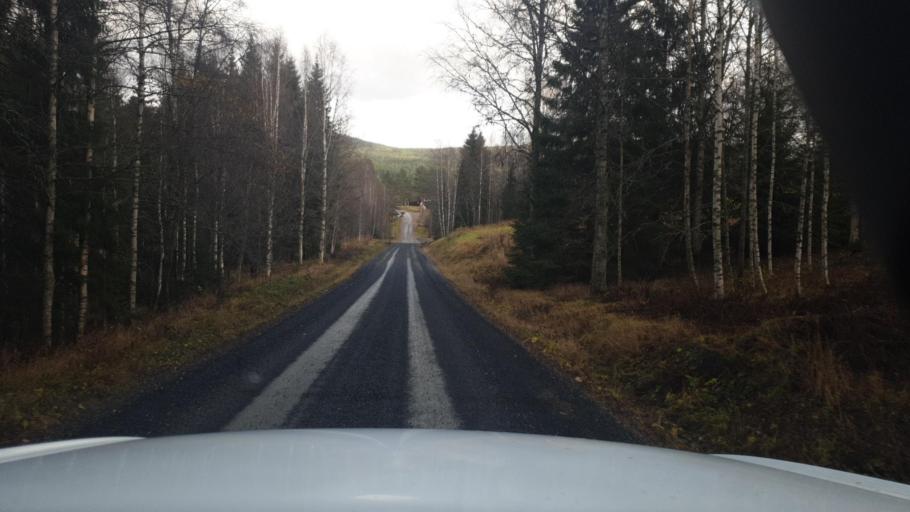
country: SE
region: Vaermland
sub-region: Torsby Kommun
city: Torsby
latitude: 60.1865
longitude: 12.6636
